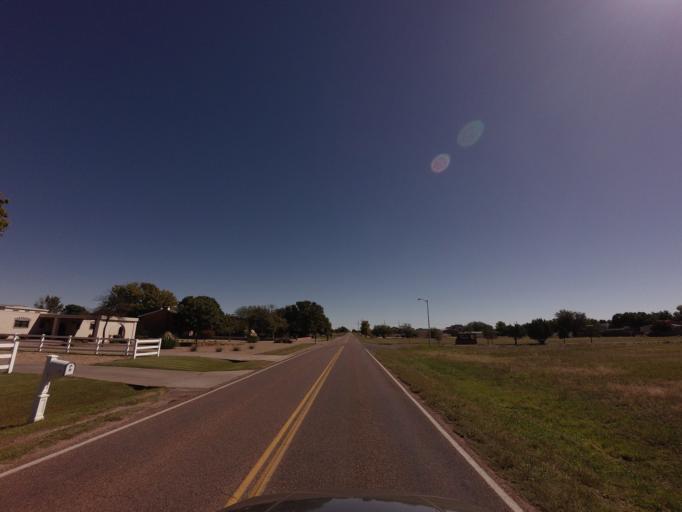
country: US
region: New Mexico
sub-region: Curry County
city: Clovis
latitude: 34.4194
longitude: -103.1724
